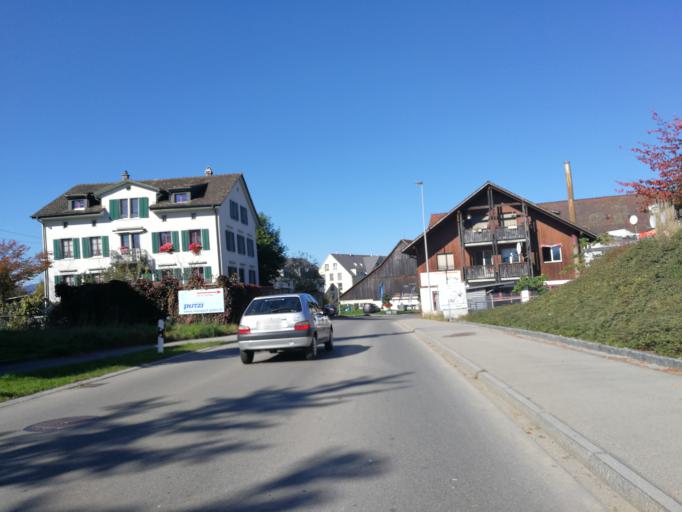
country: CH
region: Zurich
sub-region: Bezirk Hinwil
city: Binzikon
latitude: 47.2746
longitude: 8.7574
